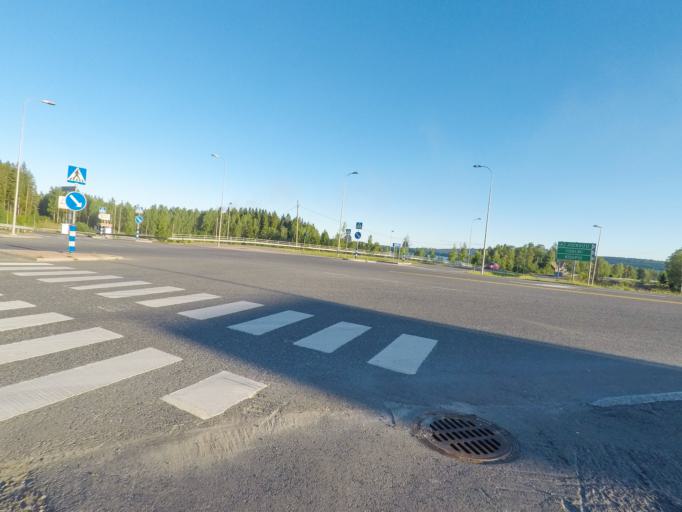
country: FI
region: Northern Savo
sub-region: Kuopio
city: Kuopio
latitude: 62.9581
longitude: 27.6930
